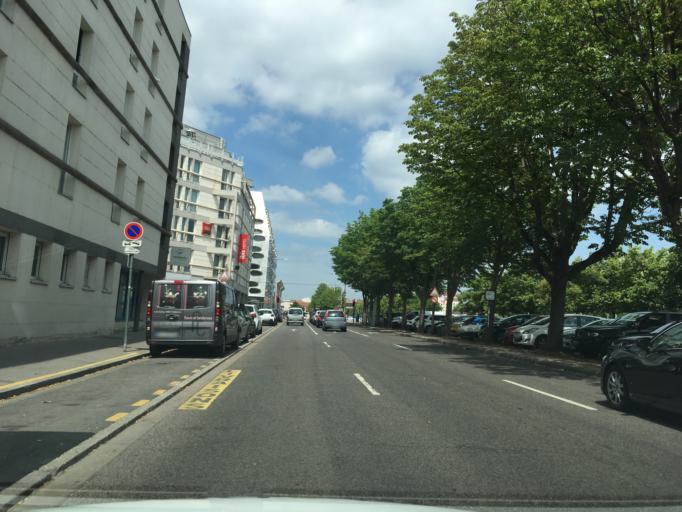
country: FR
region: Lorraine
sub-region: Departement de Meurthe-et-Moselle
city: Nancy
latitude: 48.6930
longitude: 6.1924
